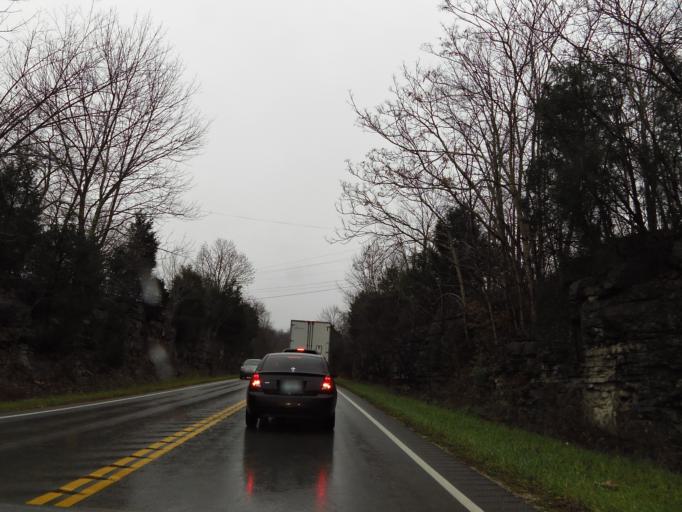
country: US
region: Kentucky
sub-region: Rockcastle County
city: Mount Vernon
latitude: 37.4181
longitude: -84.3338
